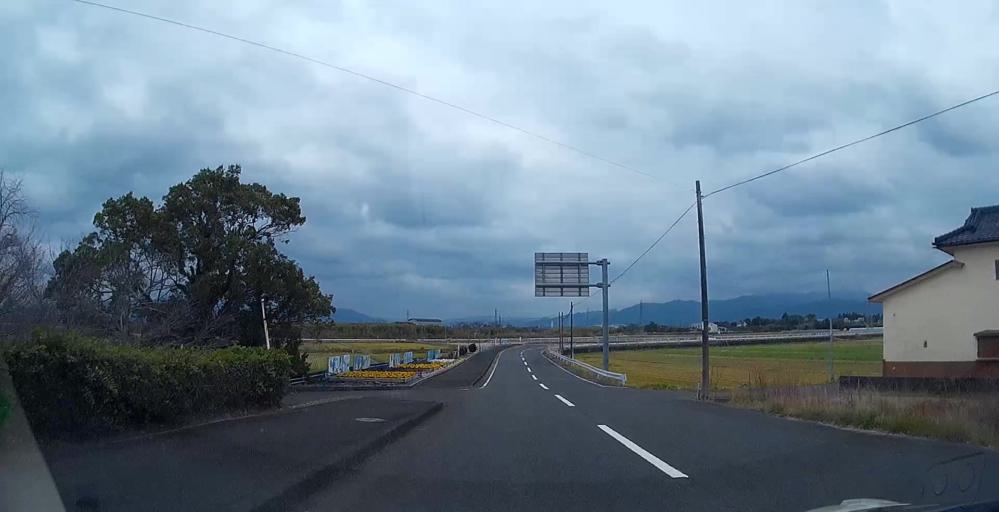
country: JP
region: Kagoshima
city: Izumi
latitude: 32.0917
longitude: 130.2748
